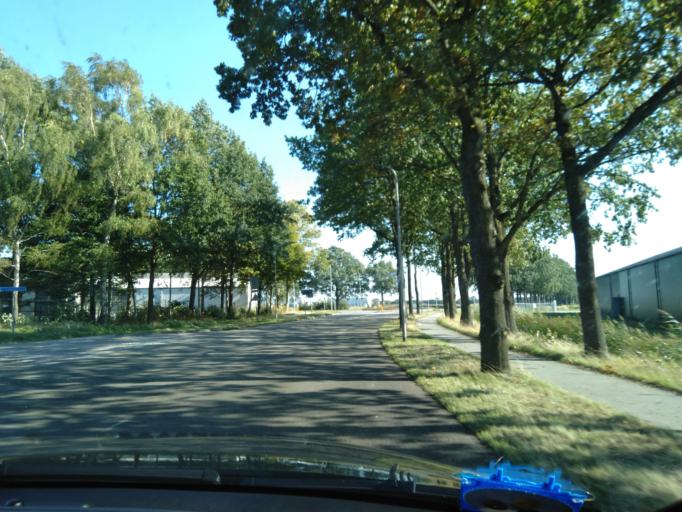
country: NL
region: Groningen
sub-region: Gemeente Veendam
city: Veendam
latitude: 53.0834
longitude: 6.8739
